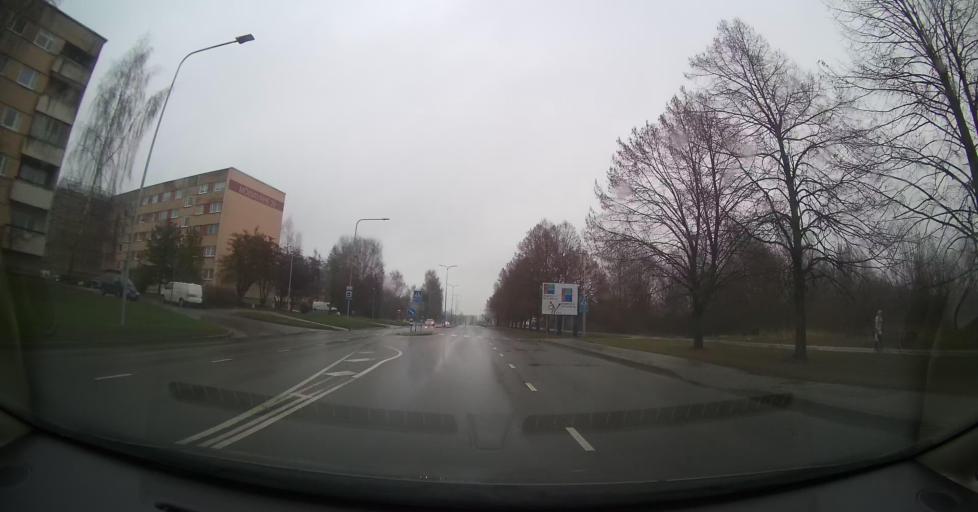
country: EE
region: Tartu
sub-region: Tartu linn
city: Tartu
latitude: 58.3688
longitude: 26.7723
